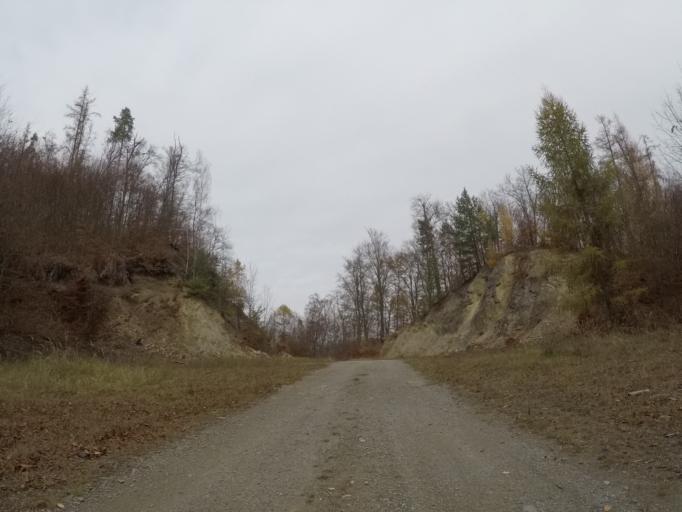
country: SK
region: Presovsky
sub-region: Okres Presov
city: Presov
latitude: 48.8957
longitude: 21.1967
